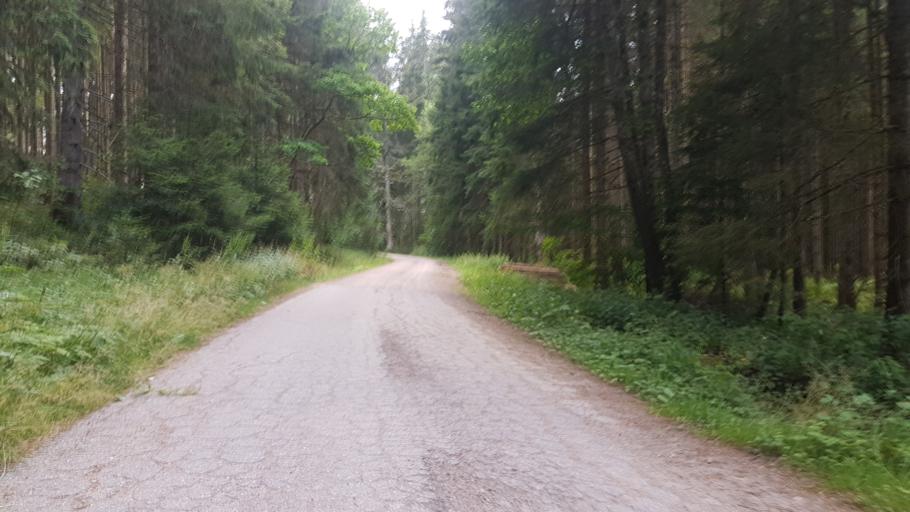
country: DE
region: Baden-Wuerttemberg
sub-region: Freiburg Region
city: Monchweiler
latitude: 48.0695
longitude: 8.4084
